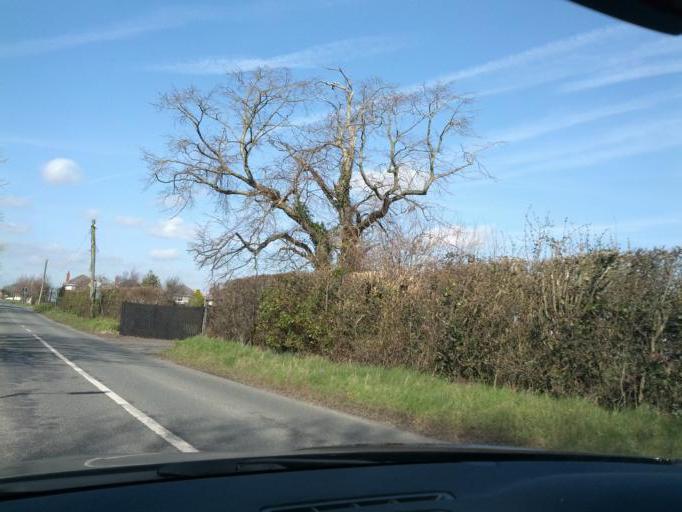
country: IE
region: Leinster
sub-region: Kildare
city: Maynooth
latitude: 53.3711
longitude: -6.5827
